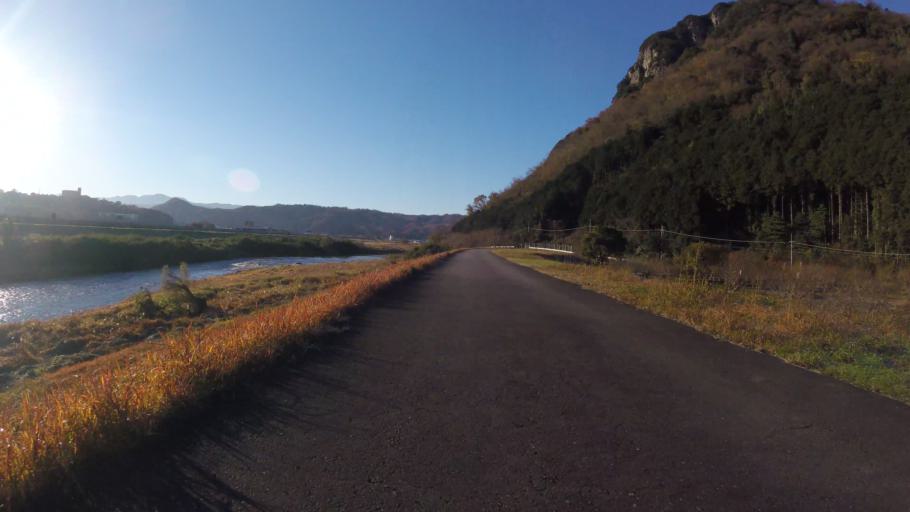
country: JP
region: Shizuoka
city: Mishima
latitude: 35.0067
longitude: 138.9353
